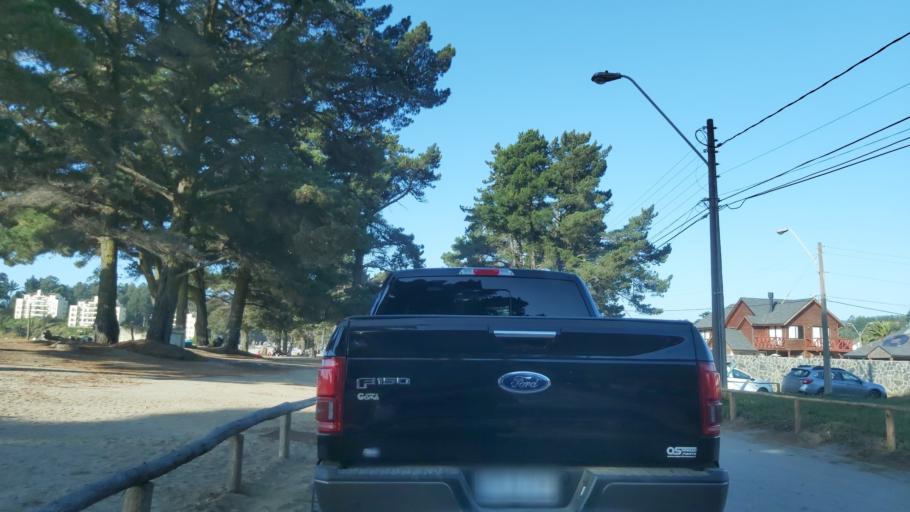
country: CL
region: Biobio
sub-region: Provincia de Concepcion
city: Tome
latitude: -36.5301
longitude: -72.9344
